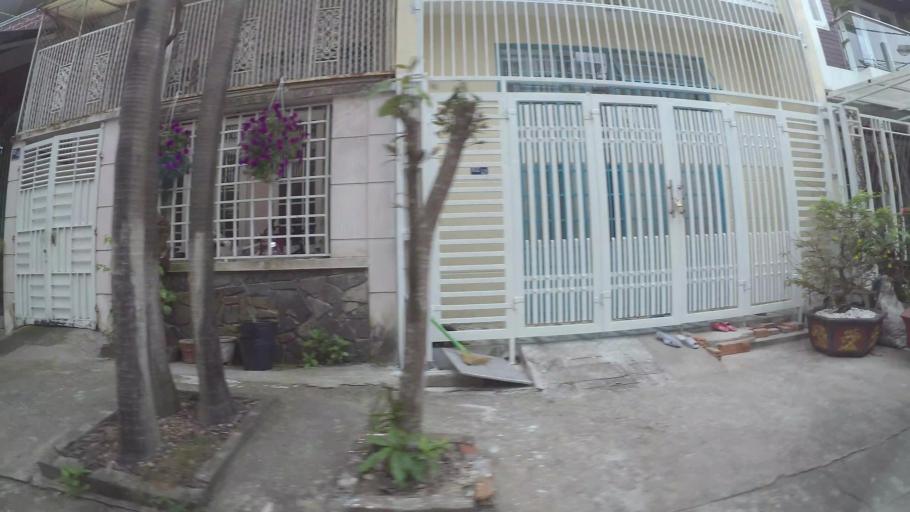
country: VN
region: Da Nang
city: Thanh Khe
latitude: 16.0586
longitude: 108.1869
